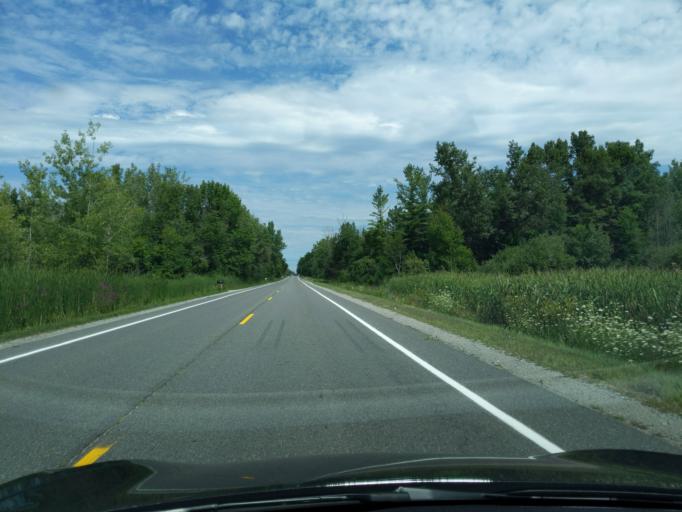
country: US
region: Michigan
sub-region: Midland County
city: Midland
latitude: 43.6032
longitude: -84.3692
